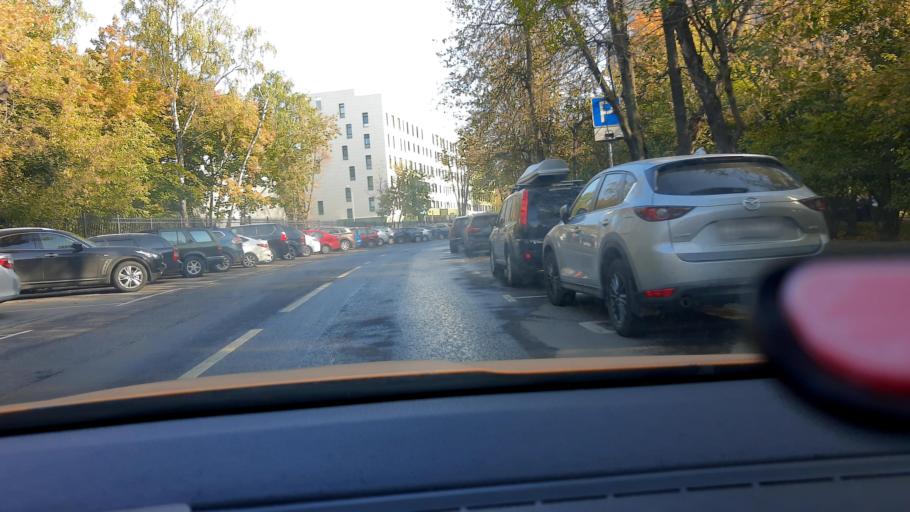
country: RU
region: Moskovskaya
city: Khoroshevo-Mnevniki
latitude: 55.8024
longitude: 37.4857
